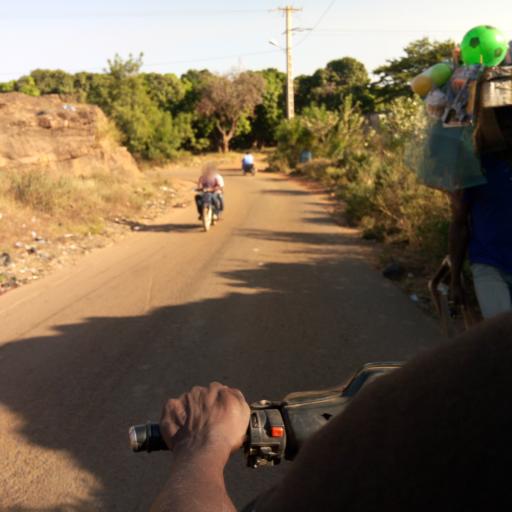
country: ML
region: Bamako
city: Bamako
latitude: 12.6601
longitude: -8.0360
